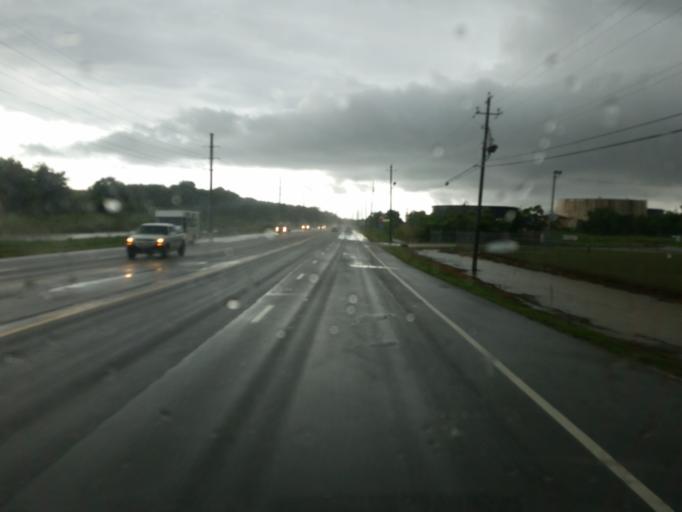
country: US
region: Alabama
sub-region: Mobile County
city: Mobile
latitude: 30.7220
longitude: -88.0365
